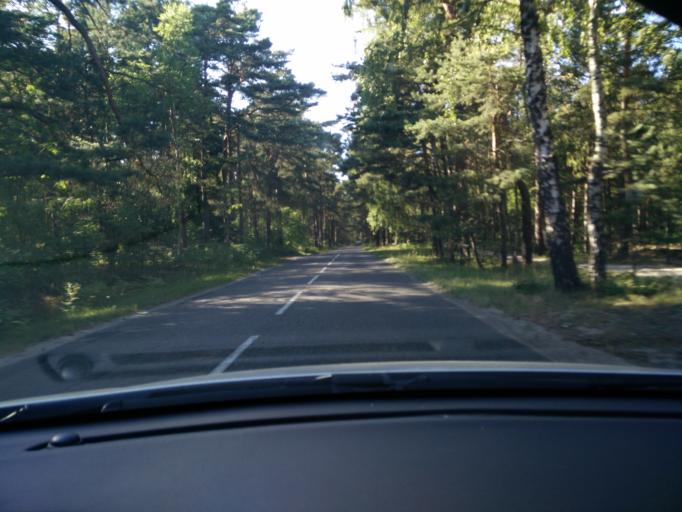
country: PL
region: Pomeranian Voivodeship
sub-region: Powiat pucki
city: Hel
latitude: 54.6385
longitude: 18.7760
